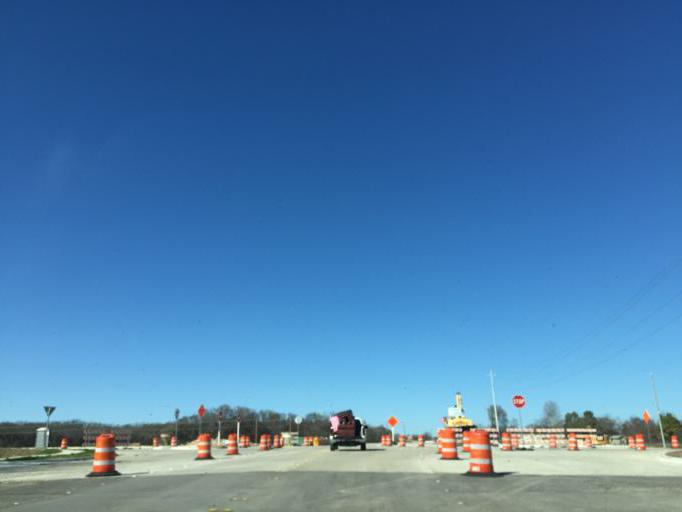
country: US
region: Texas
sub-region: Parker County
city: Hudson Oaks
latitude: 32.7472
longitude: -97.7283
